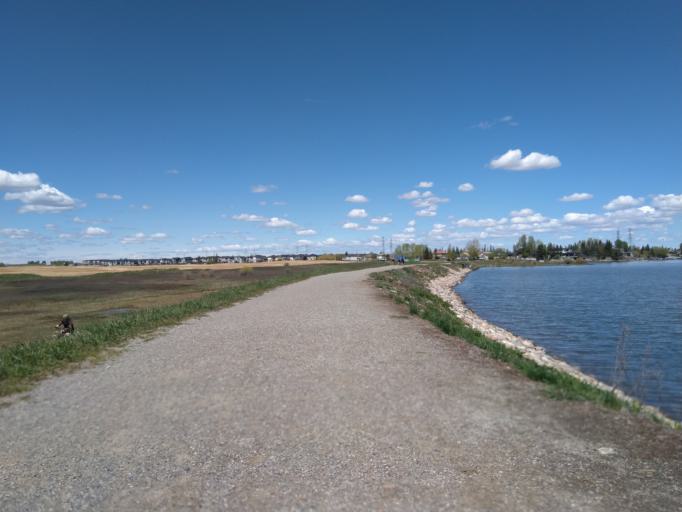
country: CA
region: Alberta
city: Chestermere
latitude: 51.0174
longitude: -113.8231
